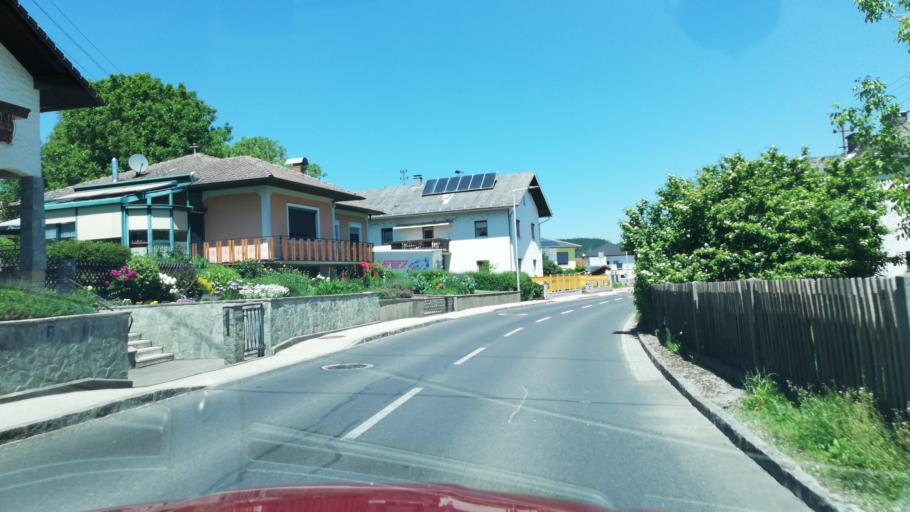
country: AT
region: Upper Austria
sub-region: Wels-Land
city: Offenhausen
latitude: 48.1511
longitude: 13.8323
